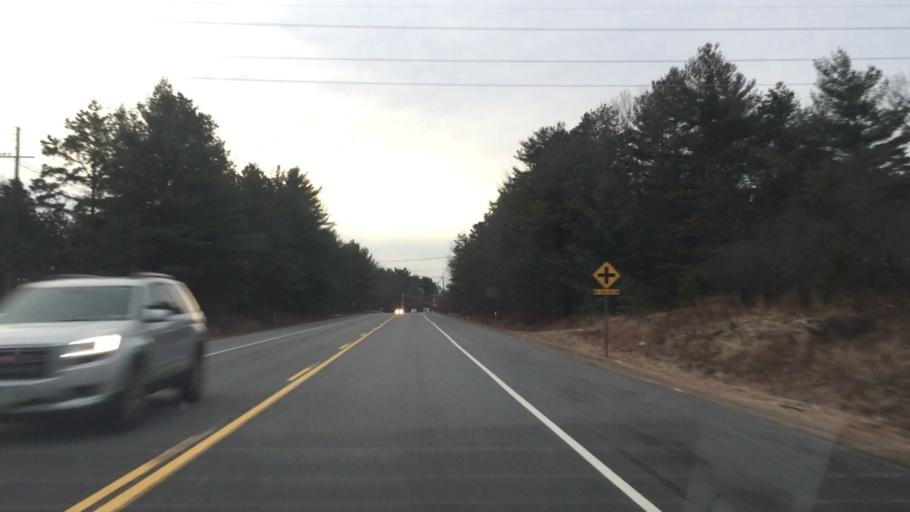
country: US
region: New Hampshire
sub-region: Hillsborough County
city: Pelham
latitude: 42.7370
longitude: -71.3112
